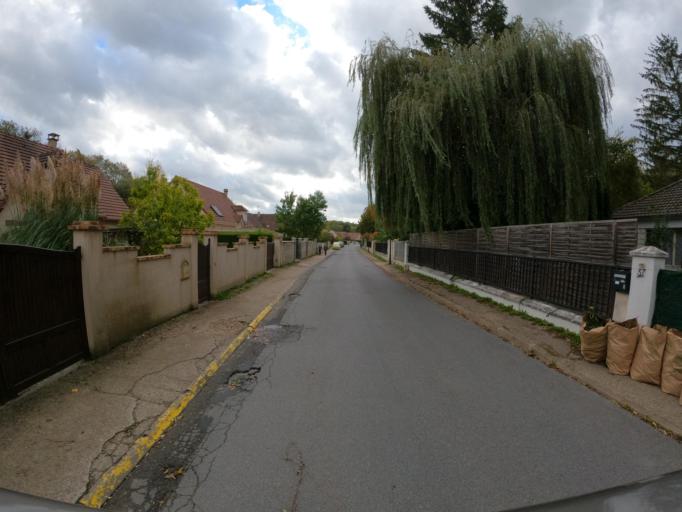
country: FR
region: Ile-de-France
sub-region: Departement de Seine-et-Marne
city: Coupvray
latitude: 48.8994
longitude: 2.7966
